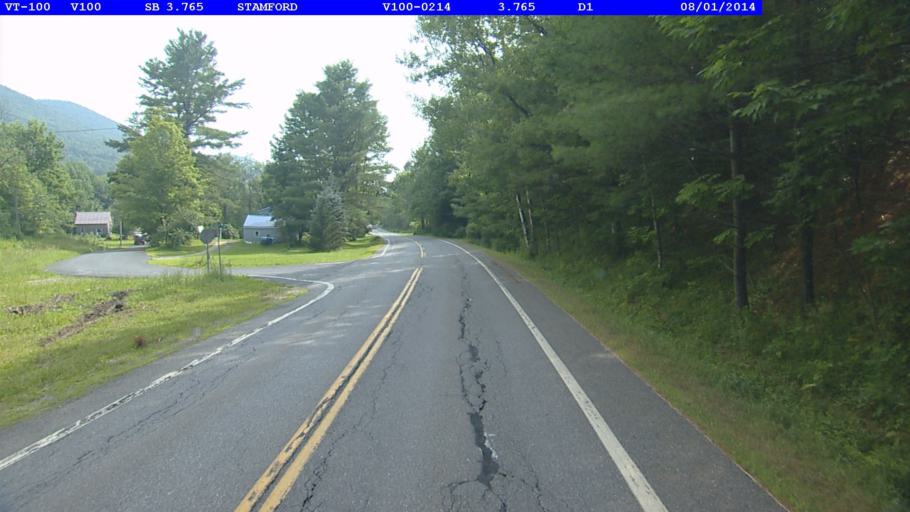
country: US
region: Massachusetts
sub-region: Berkshire County
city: North Adams
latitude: 42.7863
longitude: -73.0386
